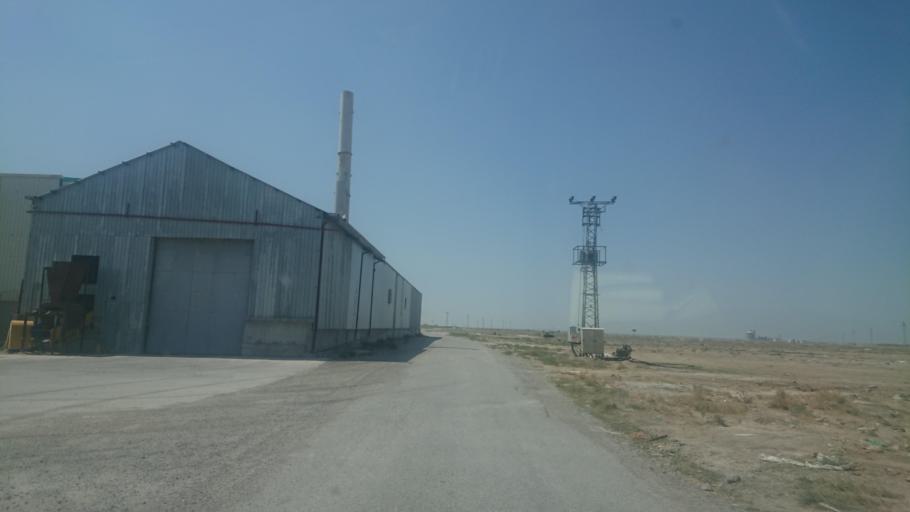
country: TR
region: Aksaray
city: Sultanhani
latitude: 38.2837
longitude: 33.7094
